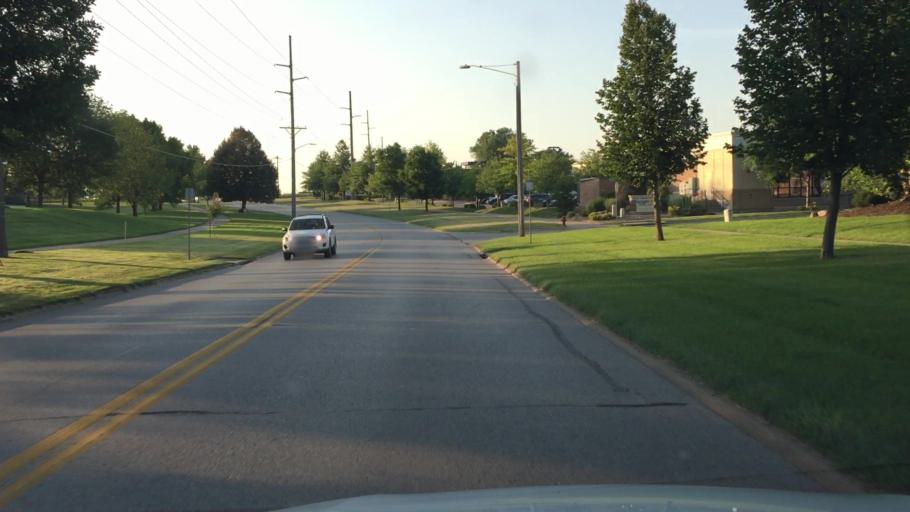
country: US
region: Iowa
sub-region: Johnson County
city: Iowa City
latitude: 41.6666
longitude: -91.4829
